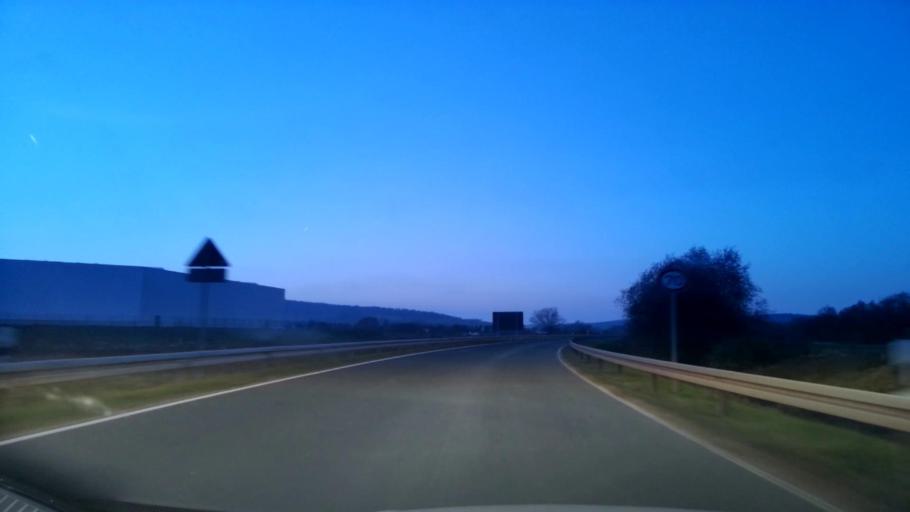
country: DE
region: Bavaria
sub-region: Upper Franconia
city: Pettstadt
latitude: 49.8301
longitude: 10.9422
